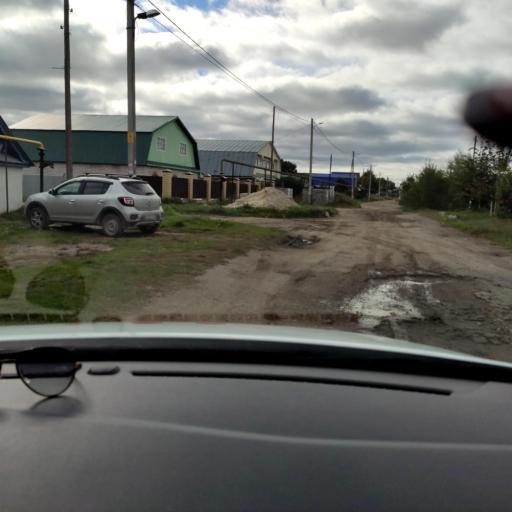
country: RU
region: Tatarstan
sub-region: Gorod Kazan'
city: Kazan
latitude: 55.7223
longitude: 49.1032
